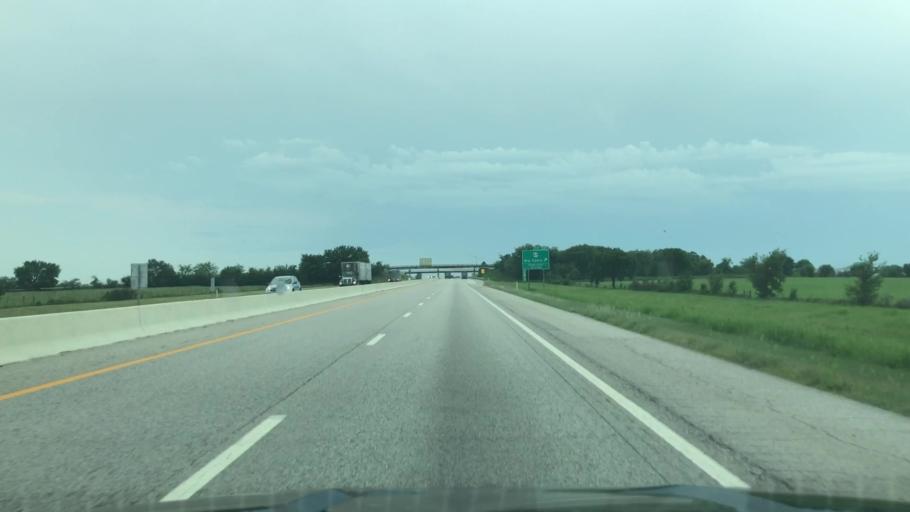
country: US
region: Oklahoma
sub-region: Craig County
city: Vinita
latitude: 36.5716
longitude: -95.2108
